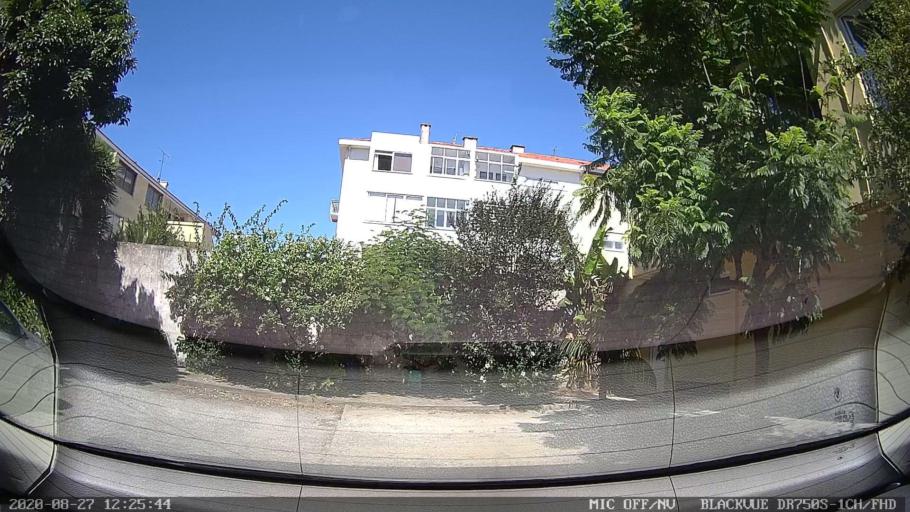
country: PT
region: Aveiro
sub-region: Aveiro
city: Aveiro
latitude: 40.6368
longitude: -8.6471
